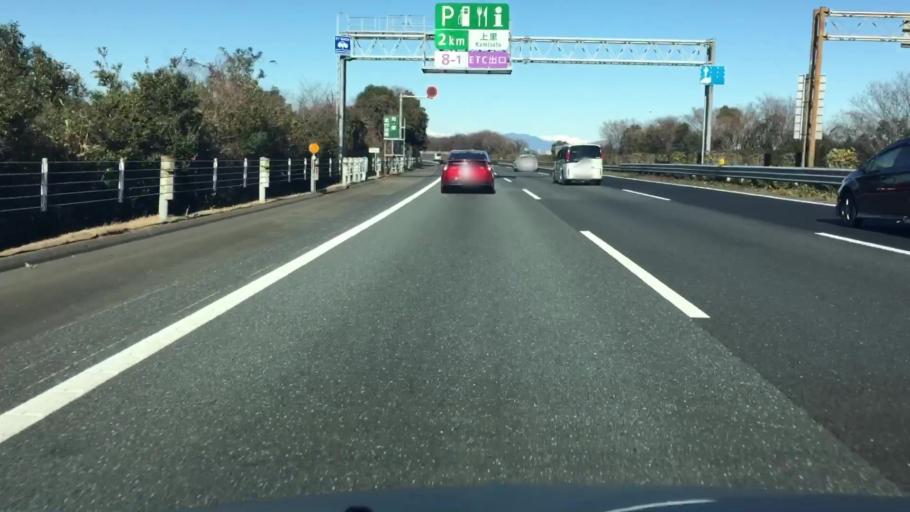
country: JP
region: Saitama
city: Honjo
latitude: 36.2424
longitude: 139.1442
